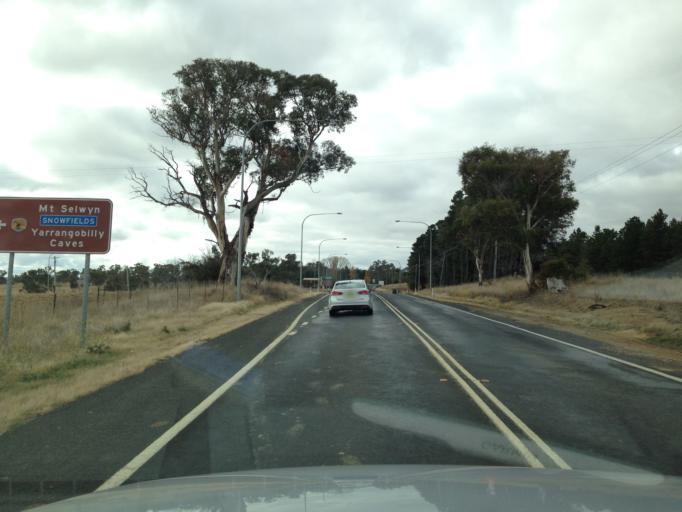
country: AU
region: New South Wales
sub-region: Cooma-Monaro
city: Cooma
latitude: -36.2478
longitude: 149.0496
